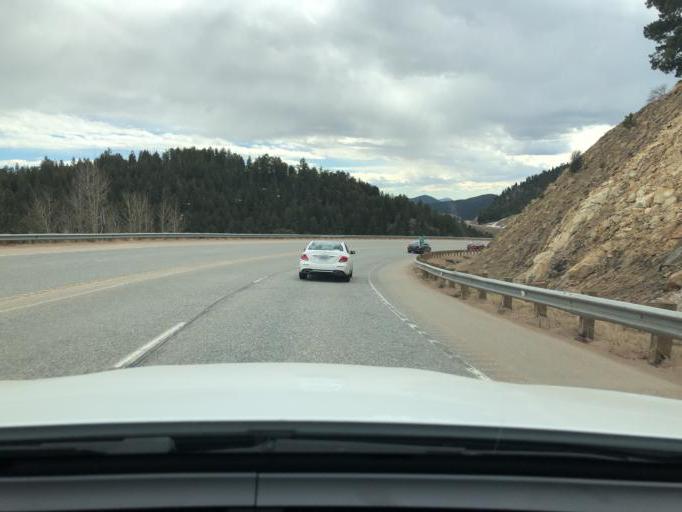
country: US
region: Colorado
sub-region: Gilpin County
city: Central City
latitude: 39.7851
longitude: -105.4841
